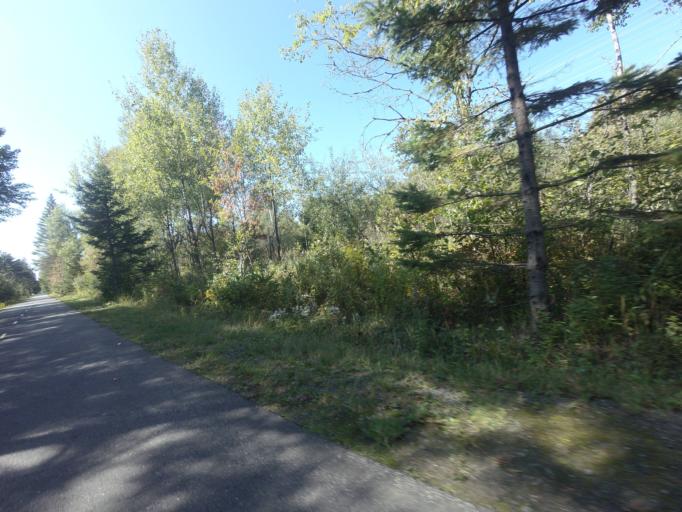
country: CA
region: Quebec
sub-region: Laurentides
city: Mont-Tremblant
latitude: 46.1287
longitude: -74.5585
